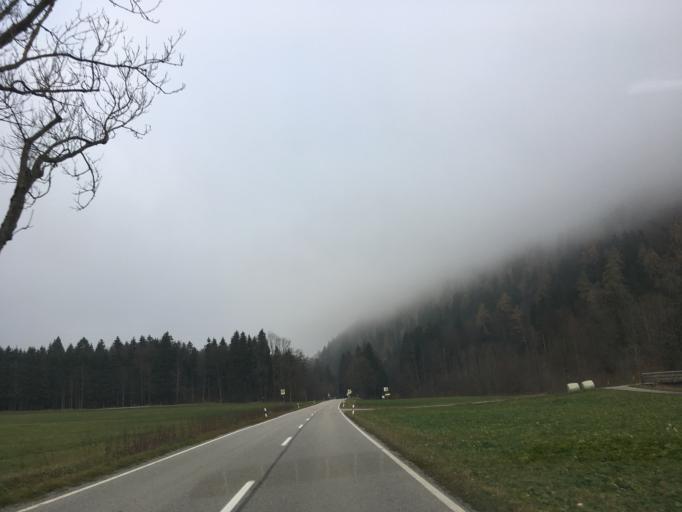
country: AT
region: Tyrol
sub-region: Politischer Bezirk Kufstein
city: Rettenschoss
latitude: 47.7082
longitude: 12.2812
